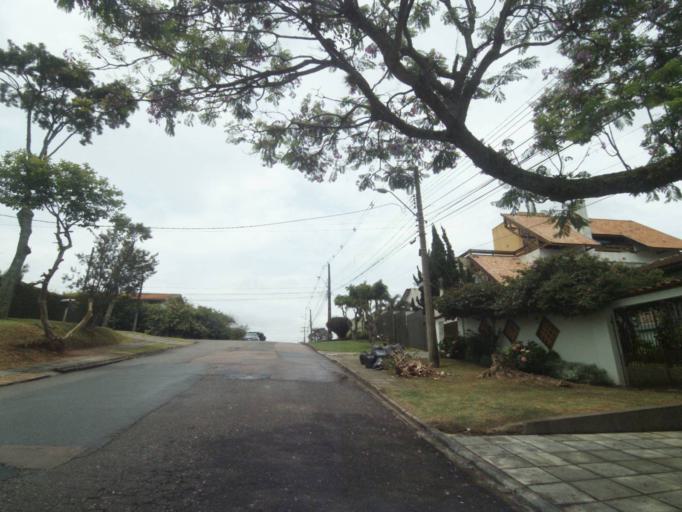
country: BR
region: Parana
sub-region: Curitiba
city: Curitiba
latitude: -25.4141
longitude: -49.2843
